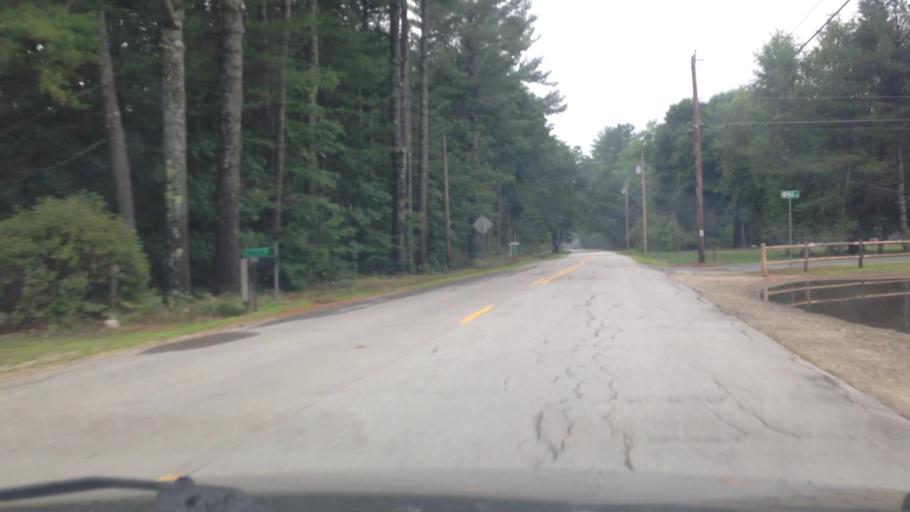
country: US
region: New Hampshire
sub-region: Cheshire County
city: Swanzey
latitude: 42.8456
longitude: -72.2674
